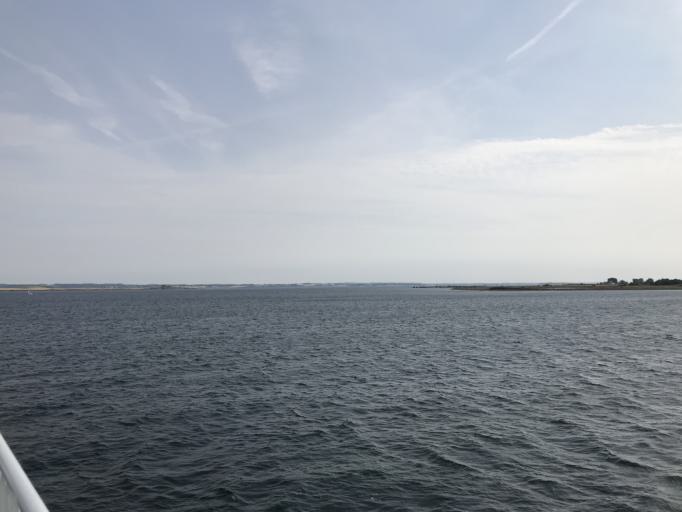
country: DK
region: South Denmark
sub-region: Faaborg-Midtfyn Kommune
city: Faaborg
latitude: 55.0363
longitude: 10.2267
